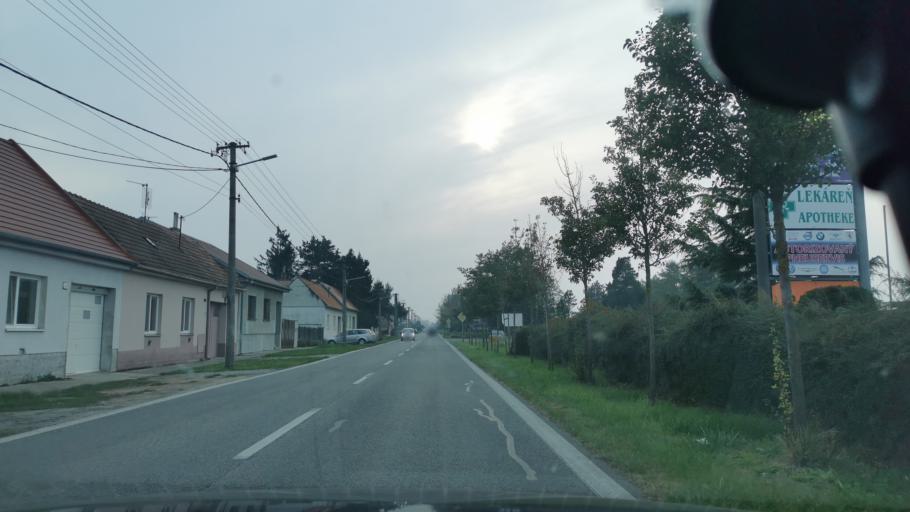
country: SK
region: Trnavsky
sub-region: Okres Skalica
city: Holic
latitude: 48.7881
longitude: 17.1198
